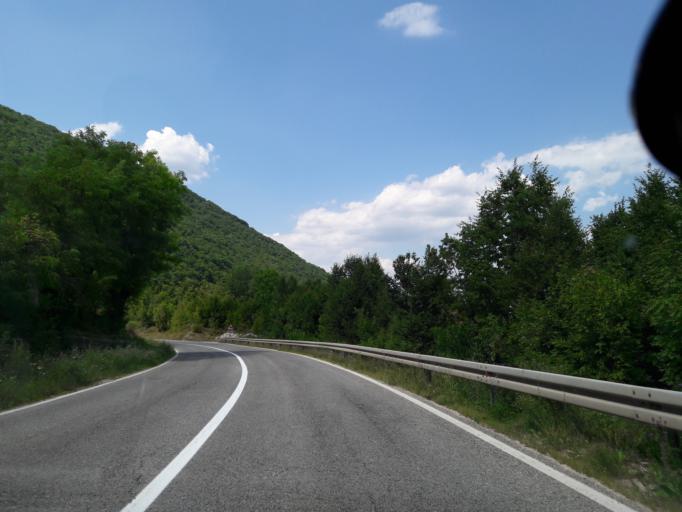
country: BA
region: Republika Srpska
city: Mrkonjic Grad
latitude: 44.4989
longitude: 17.1524
